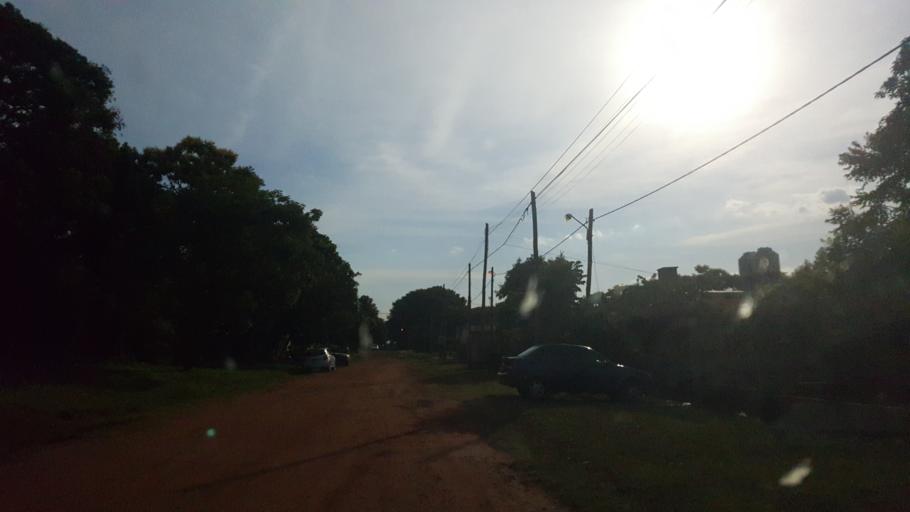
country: AR
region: Misiones
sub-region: Departamento de Capital
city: Posadas
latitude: -27.4282
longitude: -55.8872
